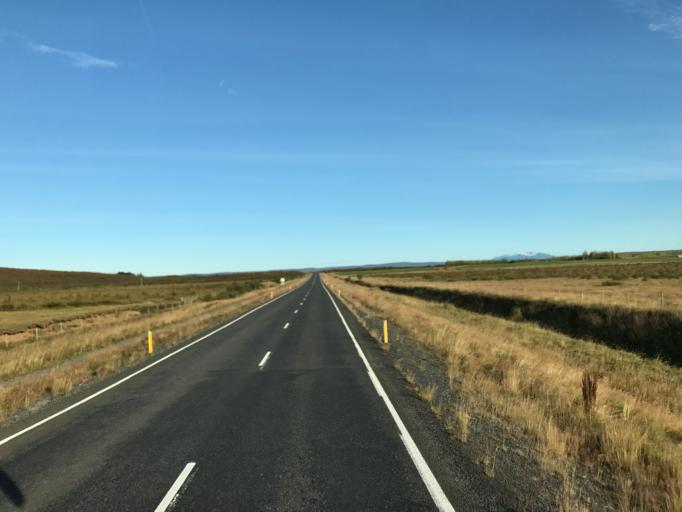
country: IS
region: South
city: Selfoss
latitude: 64.2257
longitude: -20.5998
